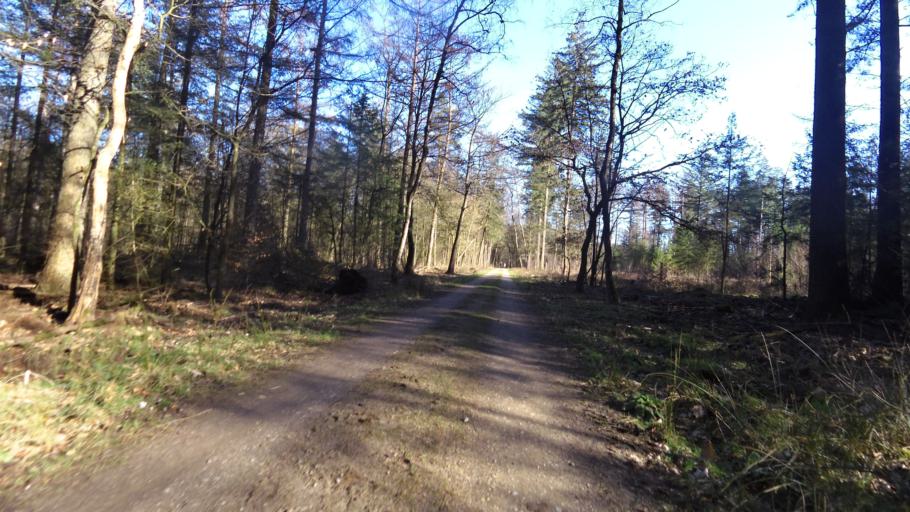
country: NL
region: Gelderland
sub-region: Gemeente Barneveld
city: Garderen
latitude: 52.2303
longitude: 5.6864
